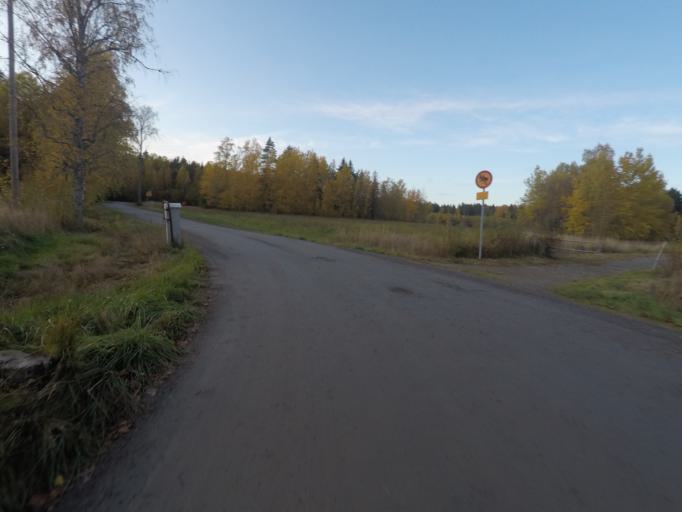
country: SE
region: OErebro
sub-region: Karlskoga Kommun
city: Karlskoga
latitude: 59.2995
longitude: 14.5116
